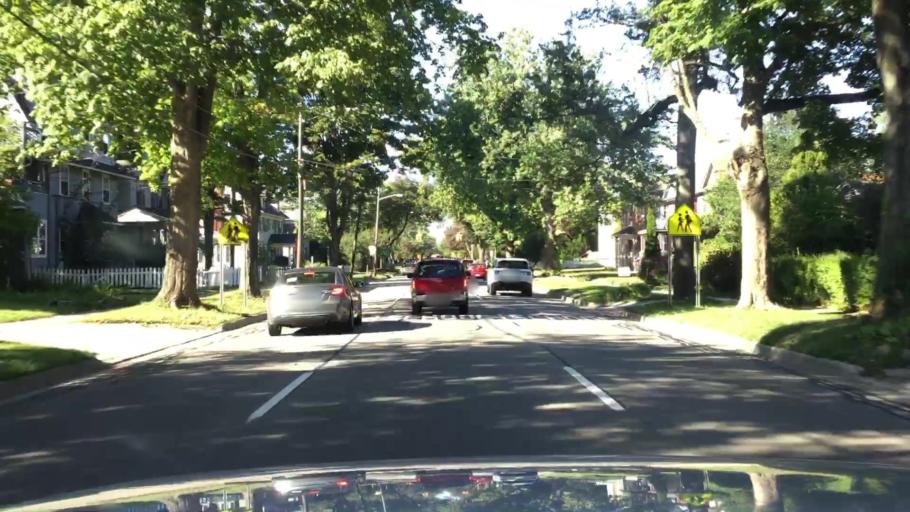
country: US
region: Michigan
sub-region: Kalamazoo County
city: Kalamazoo
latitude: 42.2826
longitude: -85.5873
